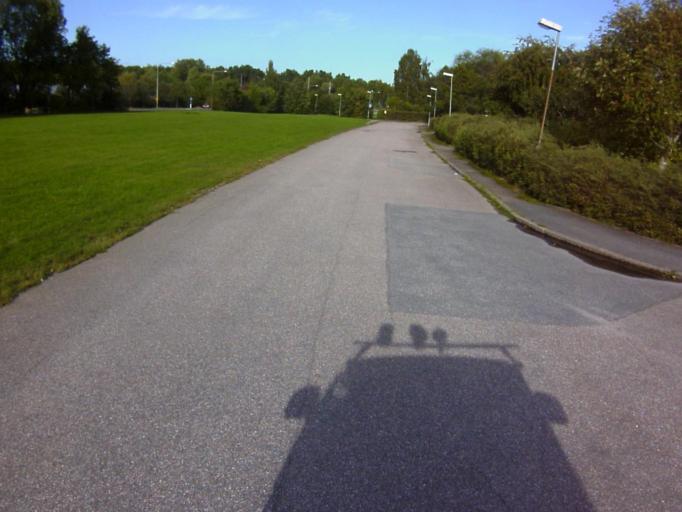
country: SE
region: Soedermanland
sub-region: Eskilstuna Kommun
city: Eskilstuna
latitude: 59.3941
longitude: 16.5397
